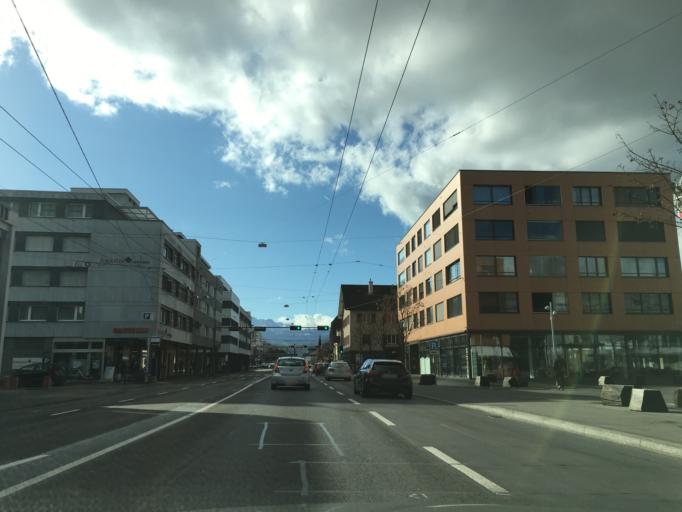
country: CH
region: Lucerne
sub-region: Lucerne-Land District
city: Ebikon
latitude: 47.0830
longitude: 8.3430
